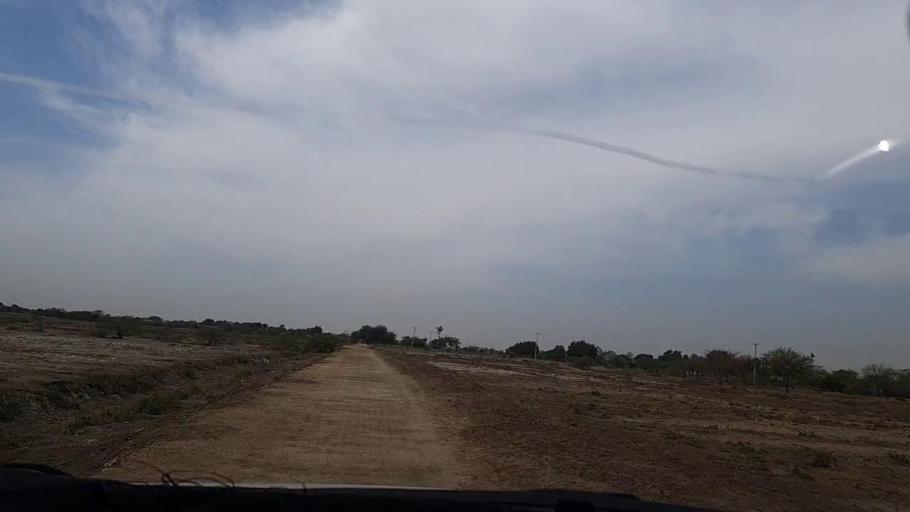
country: PK
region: Sindh
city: Dhoro Naro
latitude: 25.4506
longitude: 69.4887
